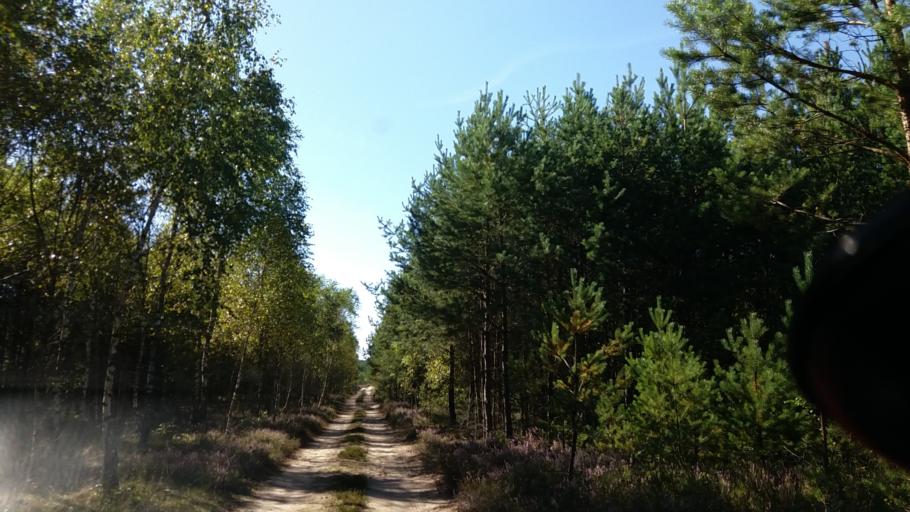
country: PL
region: West Pomeranian Voivodeship
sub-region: Powiat szczecinecki
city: Borne Sulinowo
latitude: 53.5723
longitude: 16.5057
